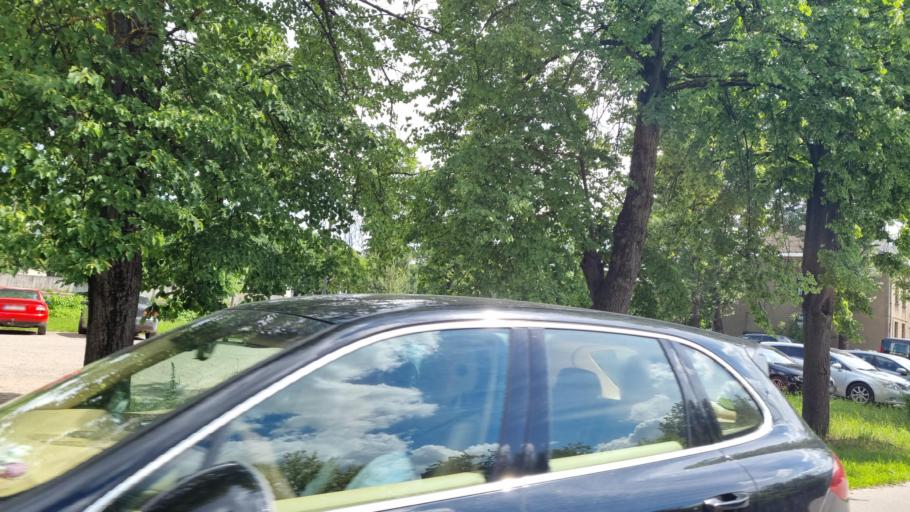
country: LV
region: Riga
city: Riga
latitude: 56.9664
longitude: 24.0958
